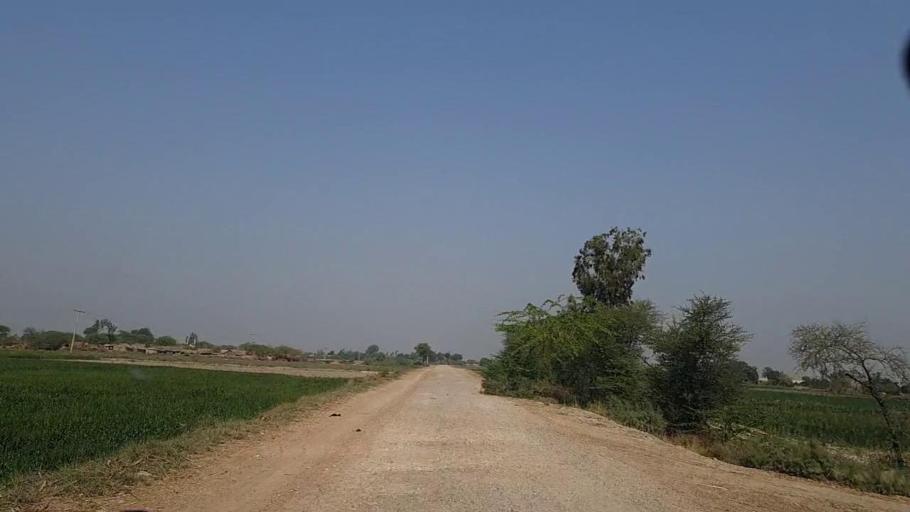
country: PK
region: Sindh
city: Mirpur Khas
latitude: 25.4951
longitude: 69.1914
